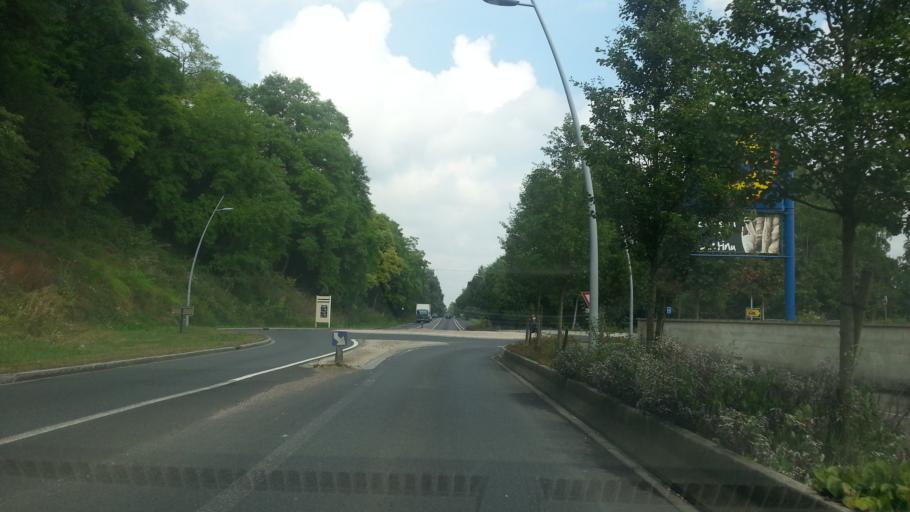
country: FR
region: Picardie
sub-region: Departement de l'Oise
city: Saint-Maximin
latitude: 49.2236
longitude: 2.4290
